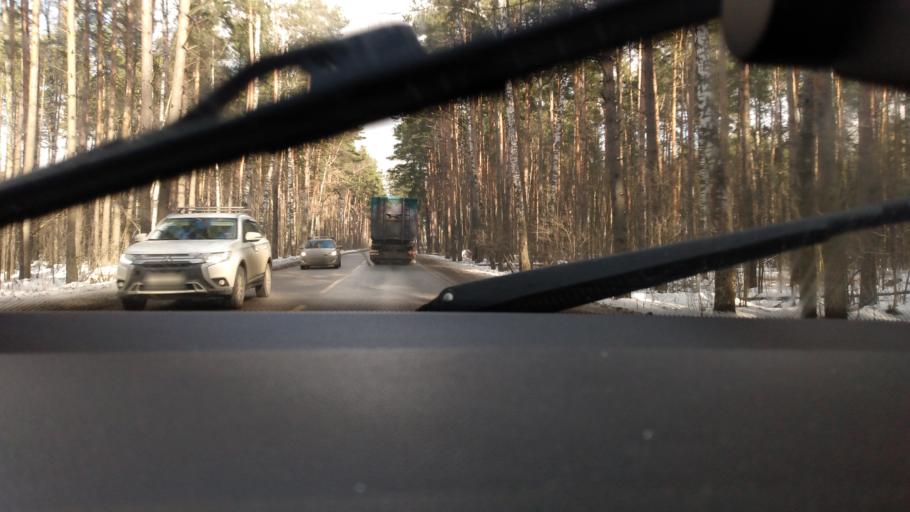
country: RU
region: Moskovskaya
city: Rodniki
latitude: 55.6748
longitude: 38.1059
